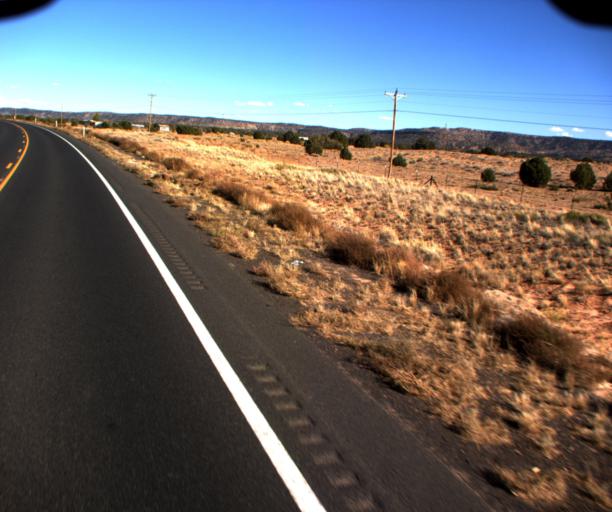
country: US
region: Arizona
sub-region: Coconino County
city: Kaibito
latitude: 36.4410
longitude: -110.7410
